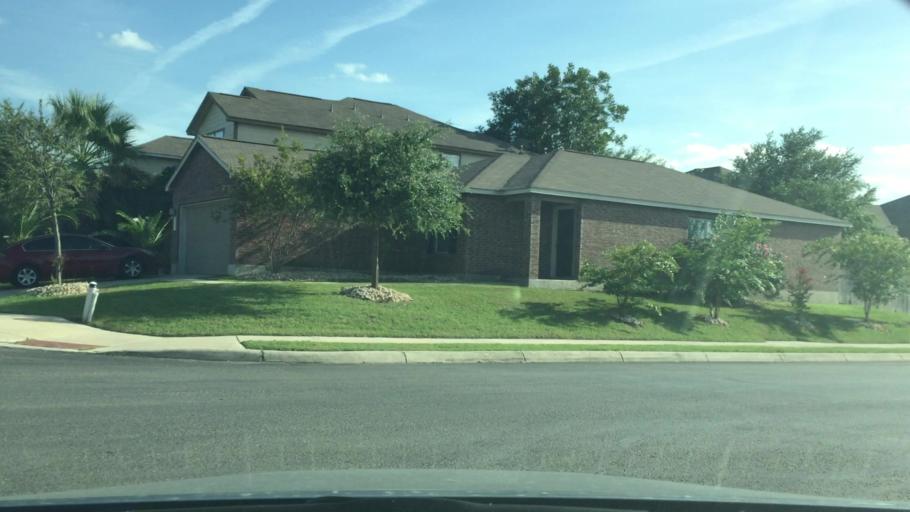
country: US
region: Texas
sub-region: Bexar County
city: Kirby
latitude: 29.4610
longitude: -98.3581
